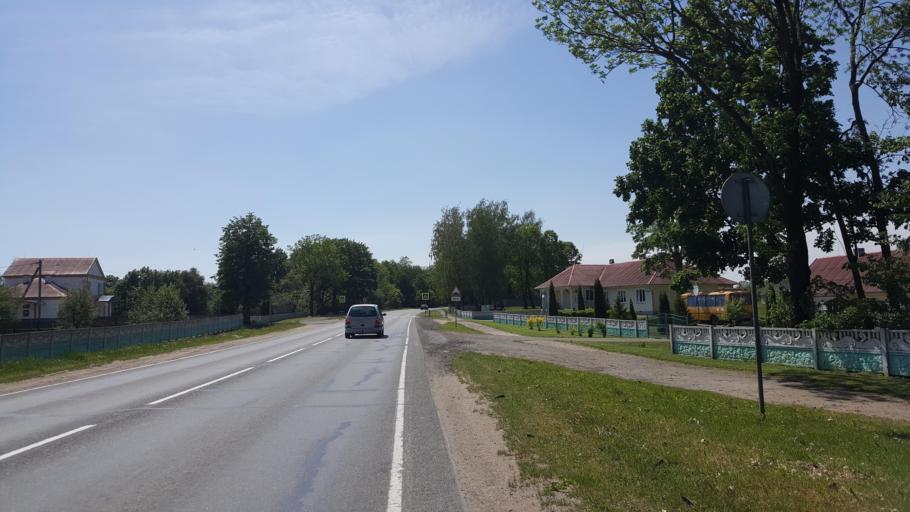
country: BY
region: Brest
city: Charnawchytsy
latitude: 52.2725
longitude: 23.7690
